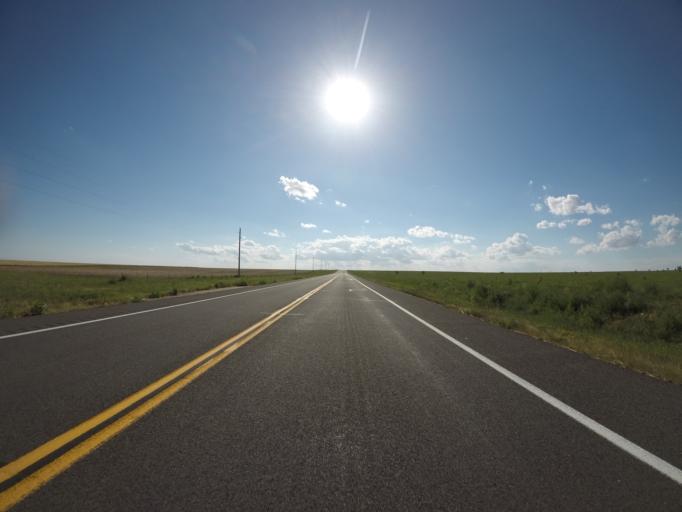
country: US
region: Colorado
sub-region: Morgan County
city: Fort Morgan
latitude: 40.6109
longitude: -103.7629
